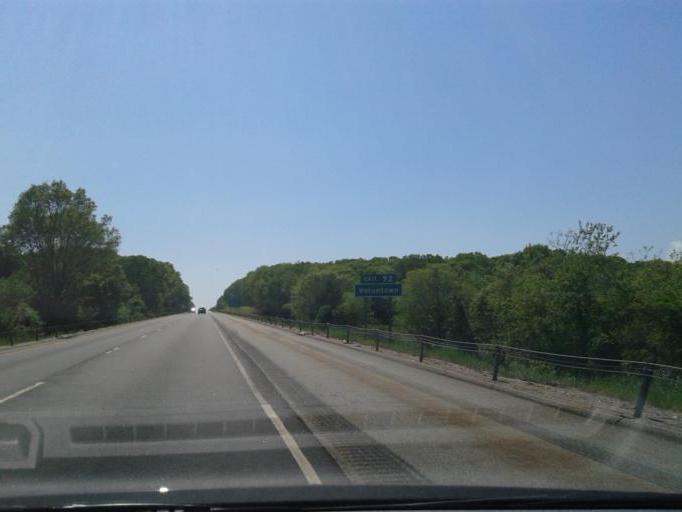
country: US
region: Rhode Island
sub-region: Washington County
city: Ashaway
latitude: 41.4265
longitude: -71.8274
